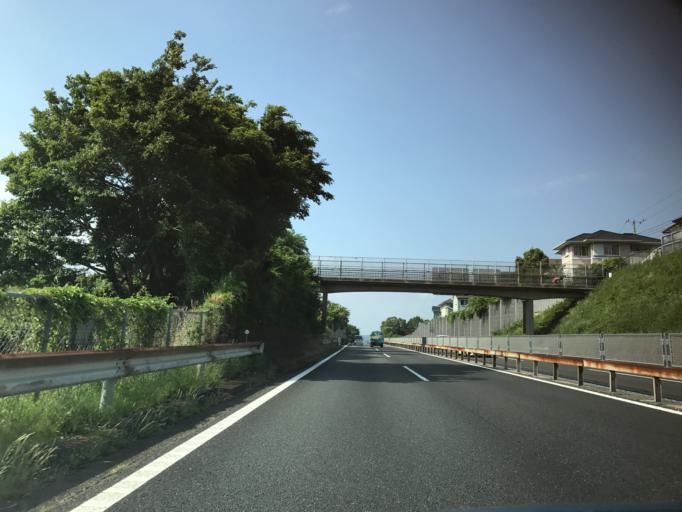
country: JP
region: Kanagawa
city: Oiso
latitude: 35.3416
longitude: 139.2964
